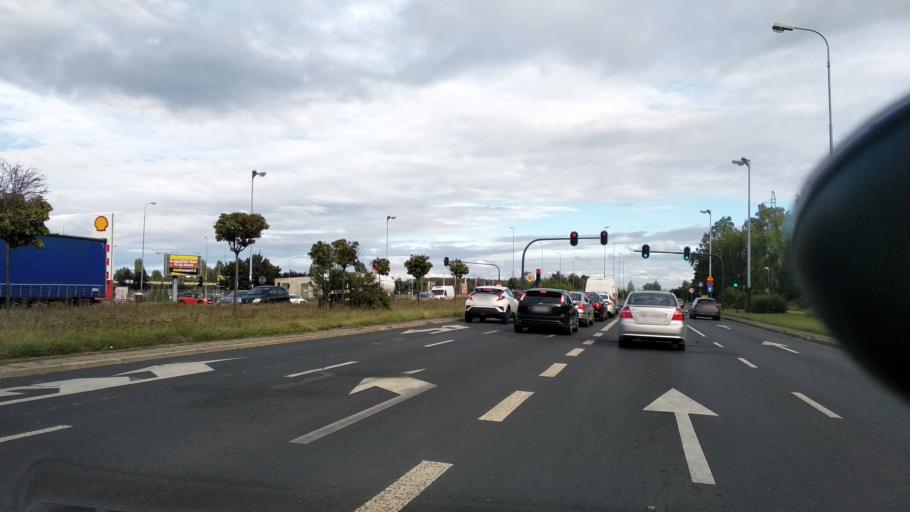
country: PL
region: Lodz Voivodeship
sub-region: Powiat lodzki wschodni
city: Andrespol
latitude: 51.7527
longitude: 19.5809
